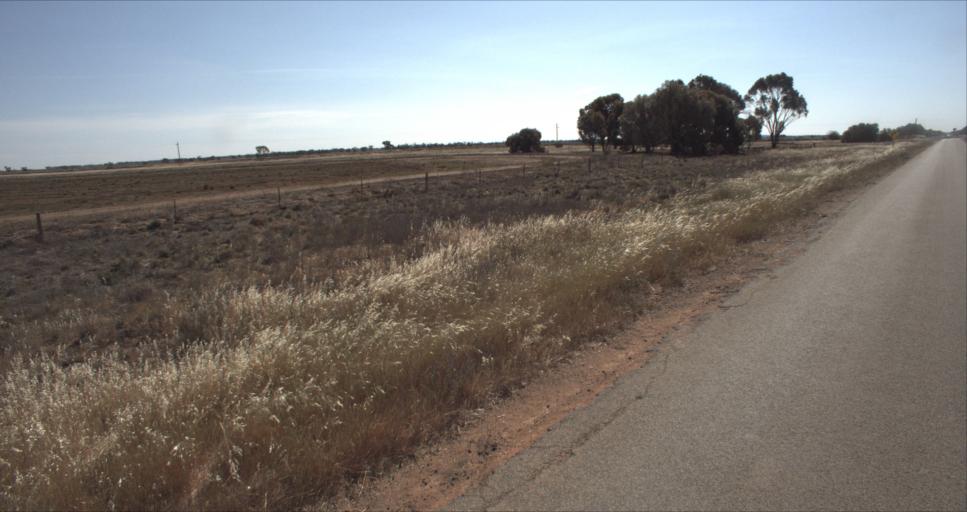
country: AU
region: New South Wales
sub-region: Leeton
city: Leeton
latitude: -34.4799
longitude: 146.3700
